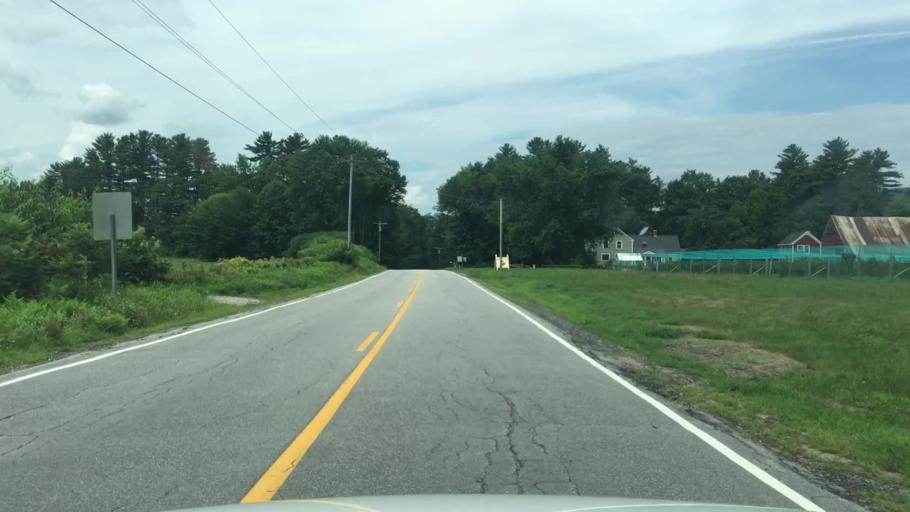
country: US
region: New Hampshire
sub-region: Grafton County
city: Rumney
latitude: 43.7835
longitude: -71.7668
